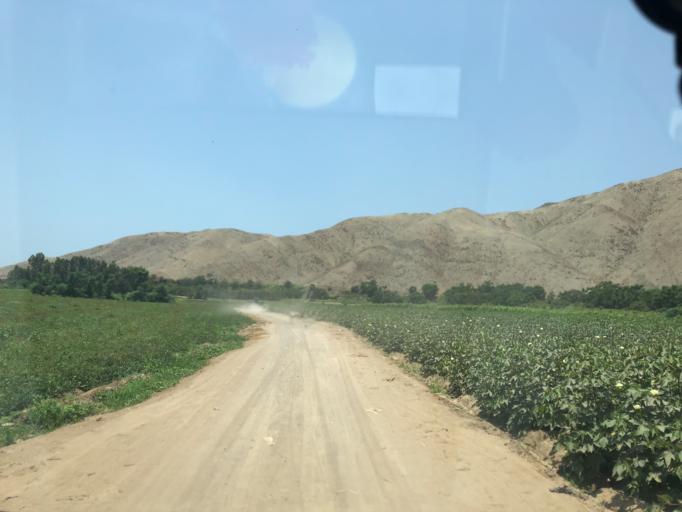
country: PE
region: Lima
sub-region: Provincia de Canete
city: Quilmana
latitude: -12.9804
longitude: -76.4284
